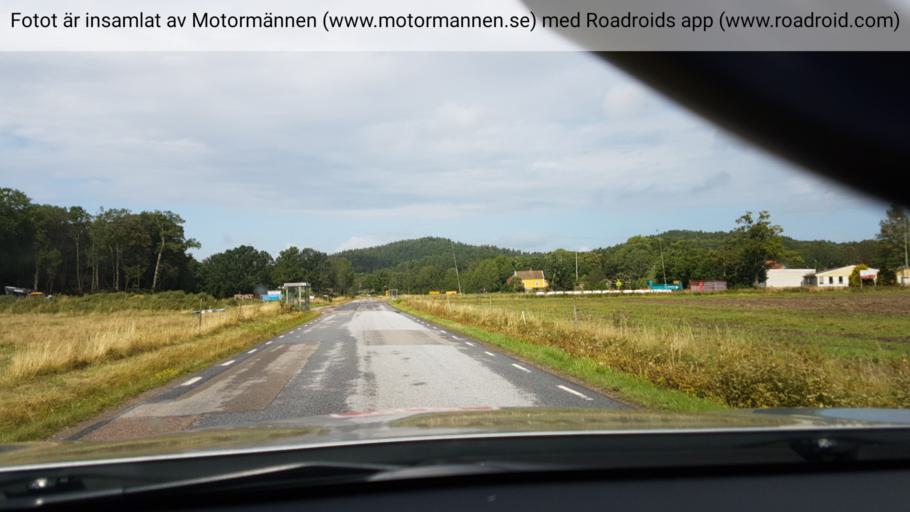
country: SE
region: Vaestra Goetaland
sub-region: Uddevalla Kommun
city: Ljungskile
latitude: 58.2311
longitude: 11.8783
